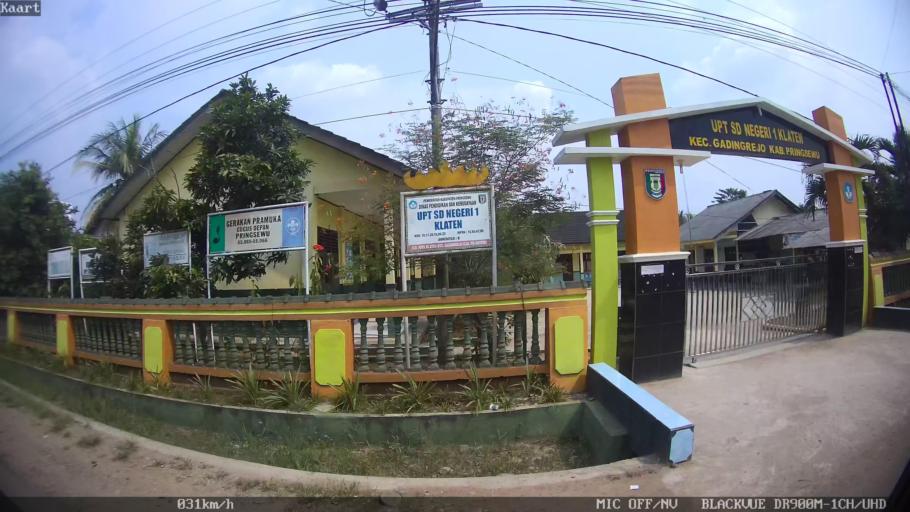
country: ID
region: Lampung
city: Gadingrejo
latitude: -5.3510
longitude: 105.0219
